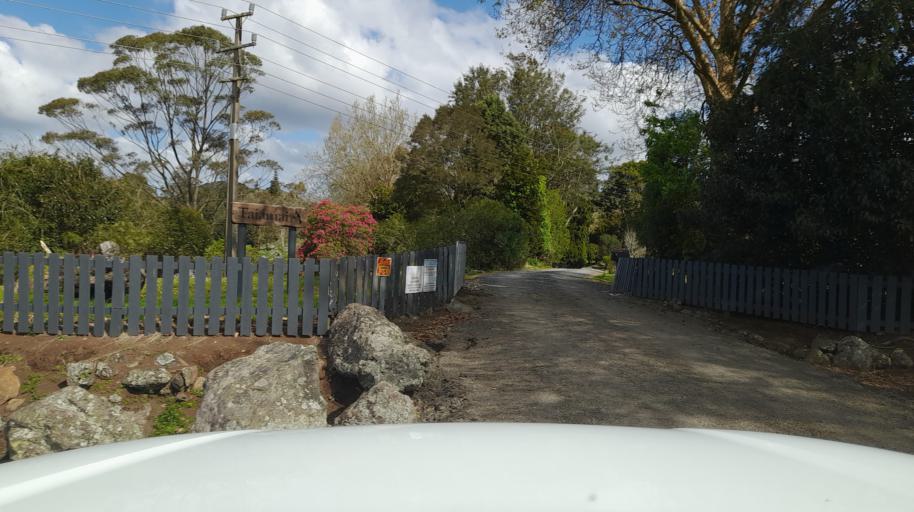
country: NZ
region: Northland
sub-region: Far North District
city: Waimate North
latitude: -35.3539
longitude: 173.8839
